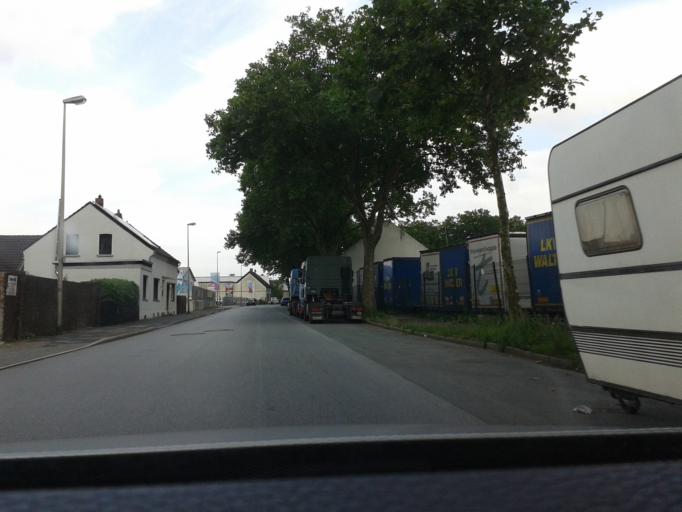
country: DE
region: North Rhine-Westphalia
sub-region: Regierungsbezirk Dusseldorf
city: Hochfeld
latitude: 51.4185
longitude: 6.7029
